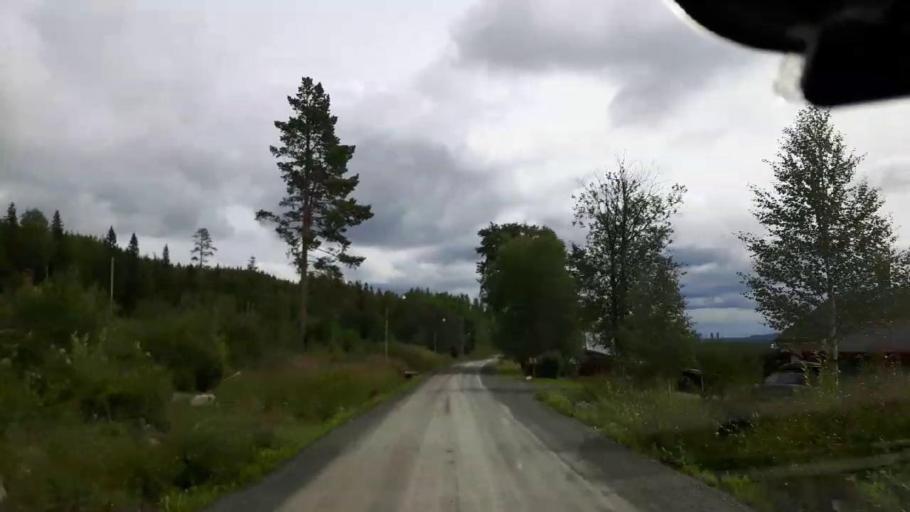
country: SE
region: Jaemtland
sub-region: Krokoms Kommun
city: Valla
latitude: 63.6239
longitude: 14.0504
